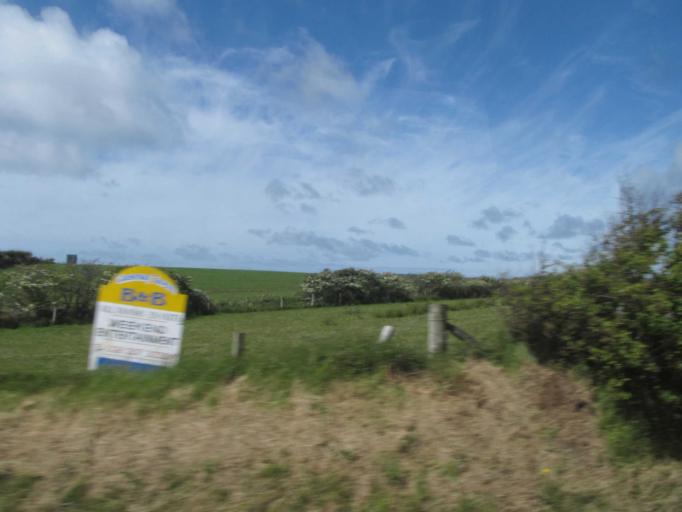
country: GB
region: Northern Ireland
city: Bushmills
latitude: 55.2202
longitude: -6.5120
